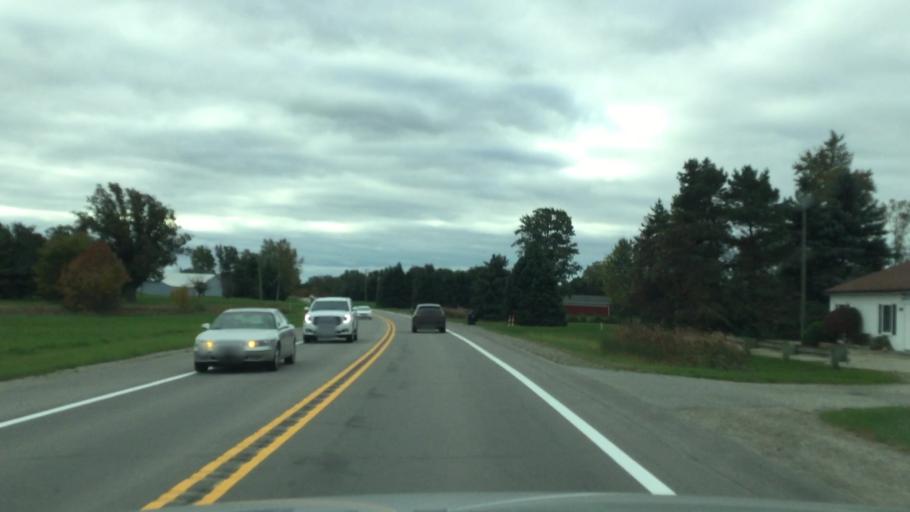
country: US
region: Michigan
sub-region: Macomb County
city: Memphis
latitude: 42.8589
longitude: -82.7664
